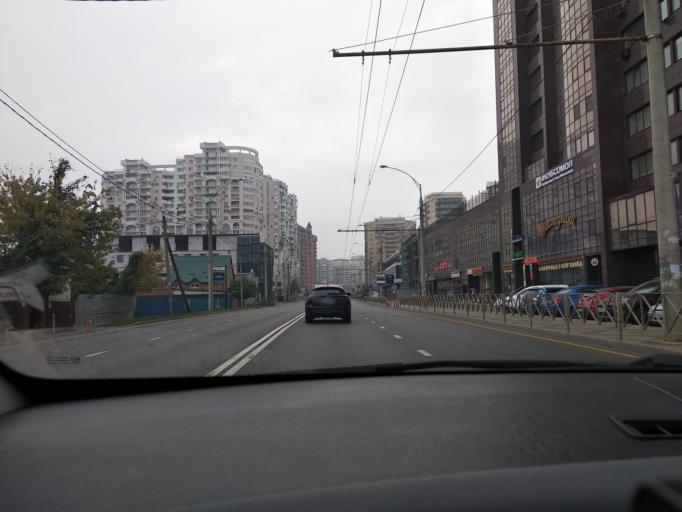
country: RU
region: Krasnodarskiy
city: Krasnodar
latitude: 45.0239
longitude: 38.9597
